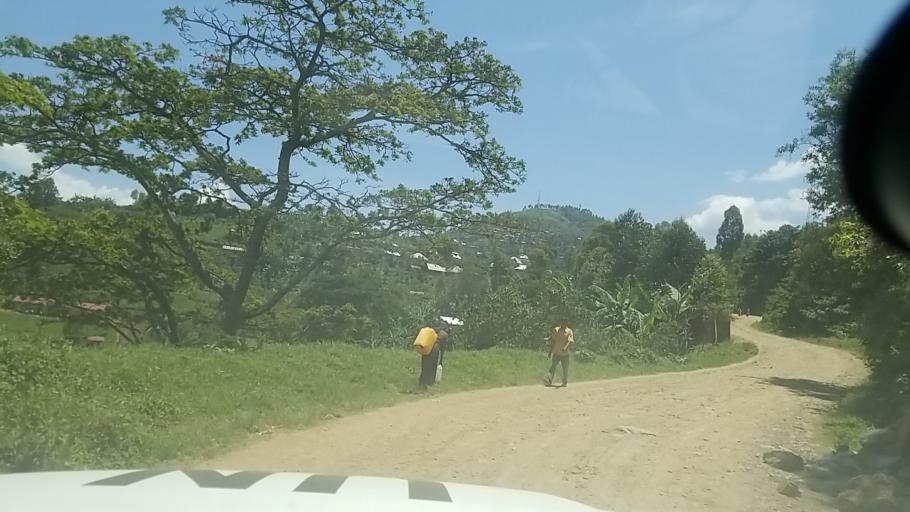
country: CD
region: Nord Kivu
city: Sake
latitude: -1.9153
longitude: 28.9506
